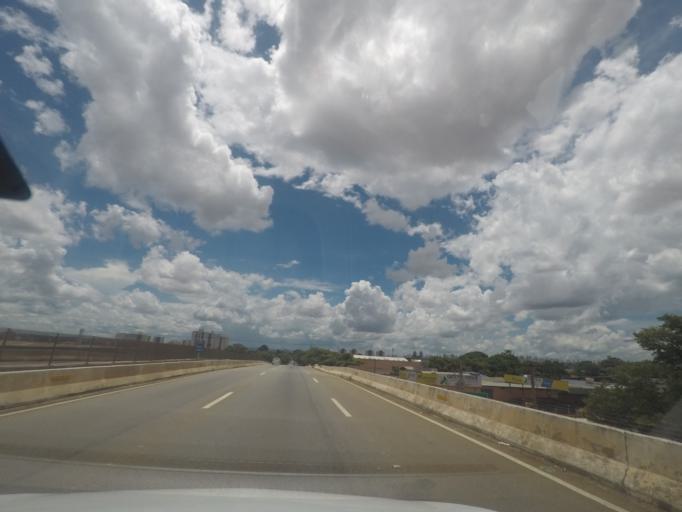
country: BR
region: Goias
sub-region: Goiania
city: Goiania
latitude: -16.7004
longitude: -49.3336
